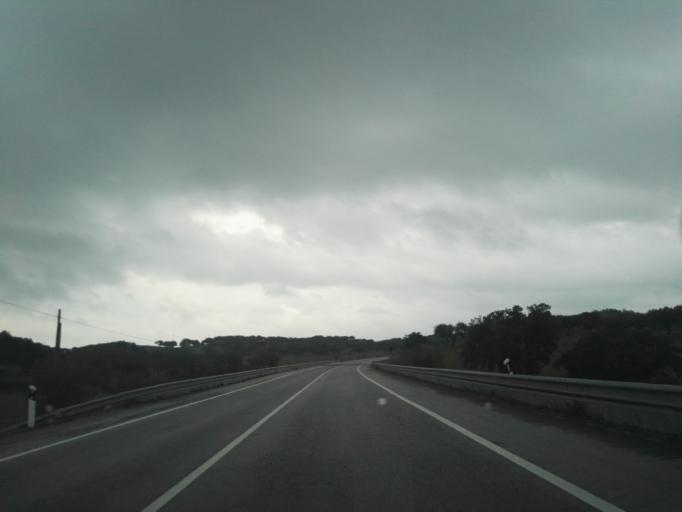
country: PT
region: Portalegre
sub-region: Portalegre
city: Alegrete
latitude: 39.1801
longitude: -7.3430
